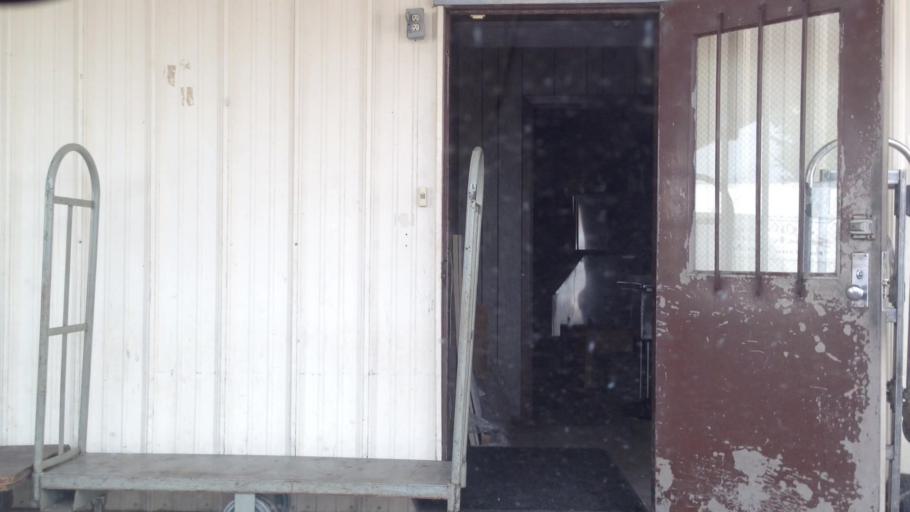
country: US
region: Louisiana
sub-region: De Soto Parish
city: Stonewall
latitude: 32.3664
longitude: -93.8217
